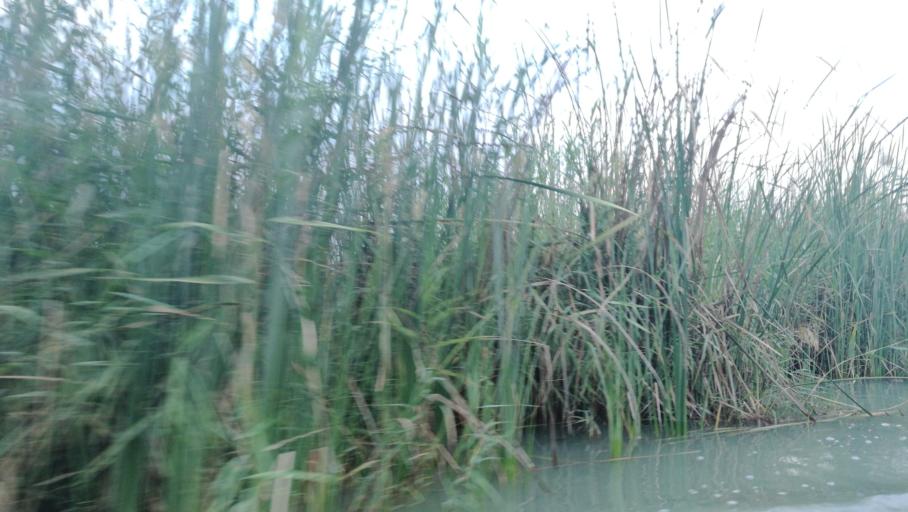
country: IQ
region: Dhi Qar
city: Al Jabayish
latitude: 30.9836
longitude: 47.0430
